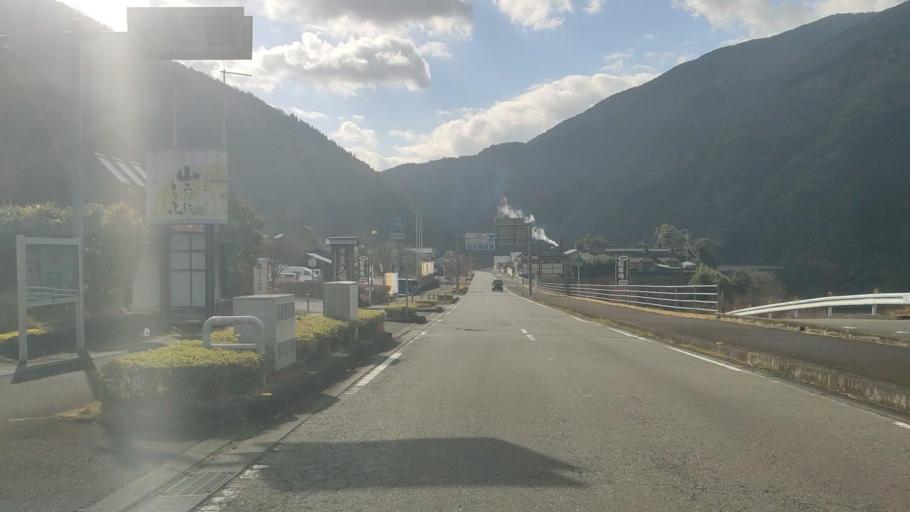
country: JP
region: Kumamoto
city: Hitoyoshi
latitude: 32.3994
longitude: 130.8265
